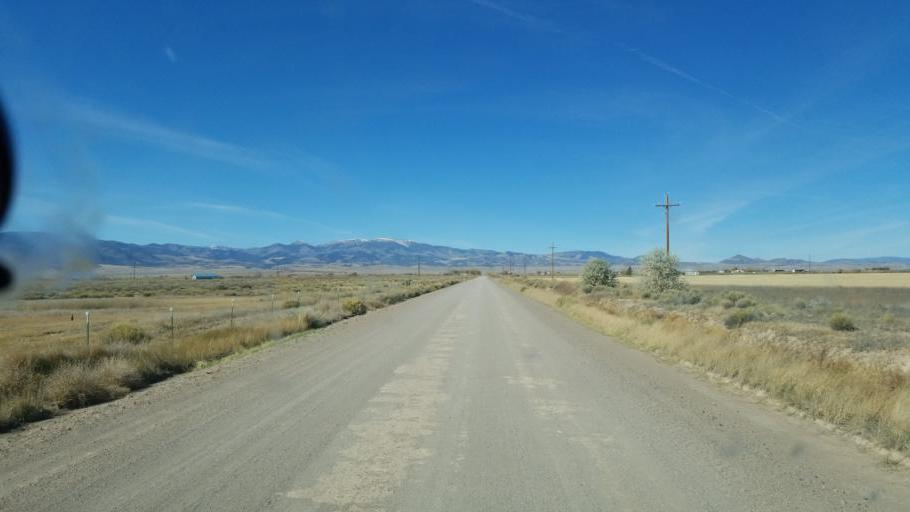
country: US
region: Colorado
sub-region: Rio Grande County
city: Monte Vista
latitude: 37.5313
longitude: -106.0864
